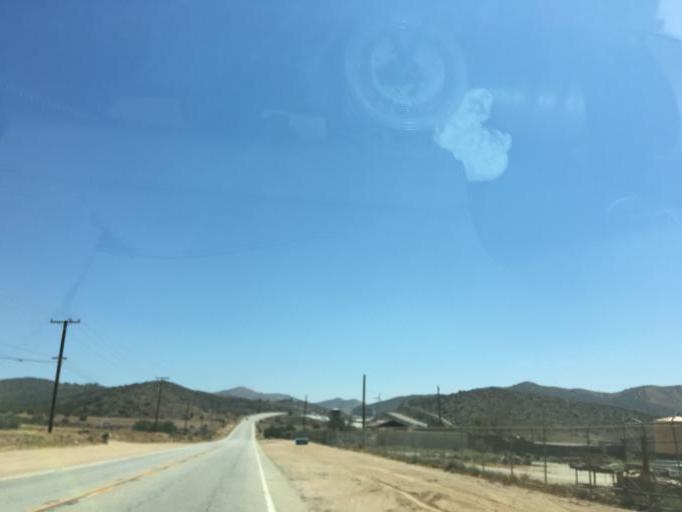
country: US
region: California
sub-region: Los Angeles County
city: Acton
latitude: 34.4933
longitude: -118.1947
